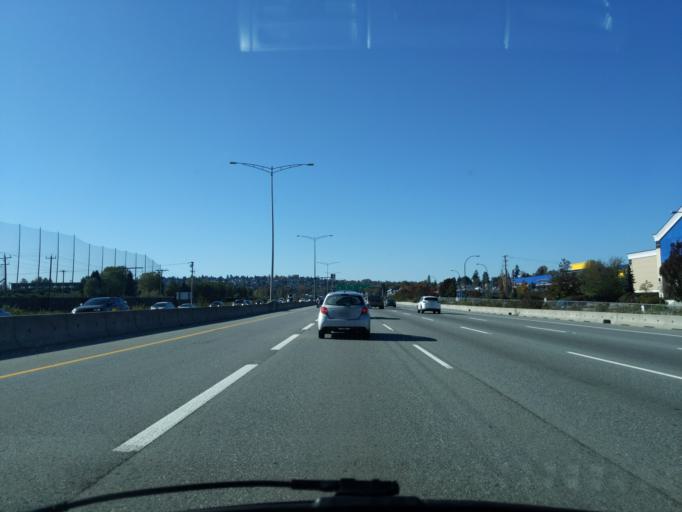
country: CA
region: British Columbia
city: Port Moody
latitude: 49.2327
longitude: -122.8627
